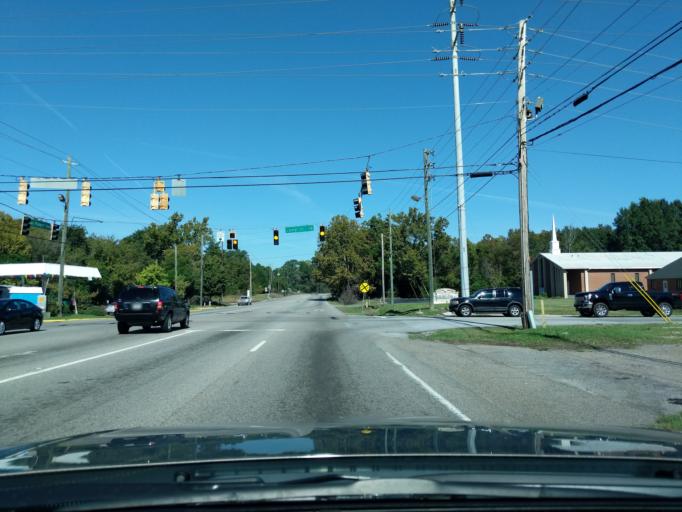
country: US
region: Georgia
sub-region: Richmond County
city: Augusta
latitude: 33.4165
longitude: -82.0069
